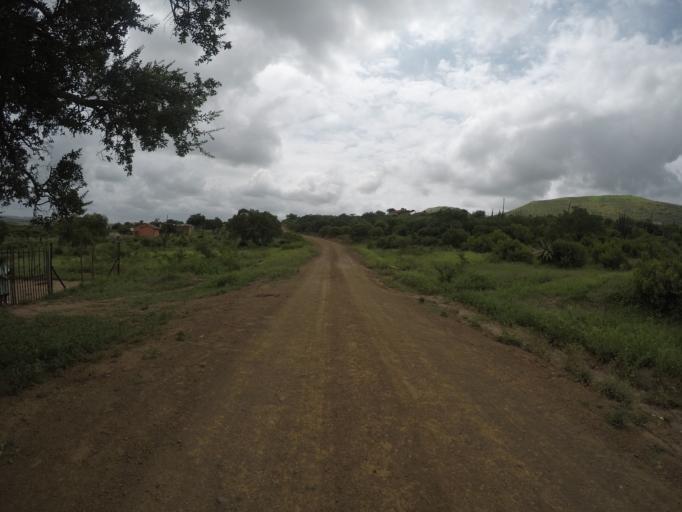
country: ZA
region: KwaZulu-Natal
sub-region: uThungulu District Municipality
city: Empangeni
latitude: -28.5818
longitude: 31.8660
